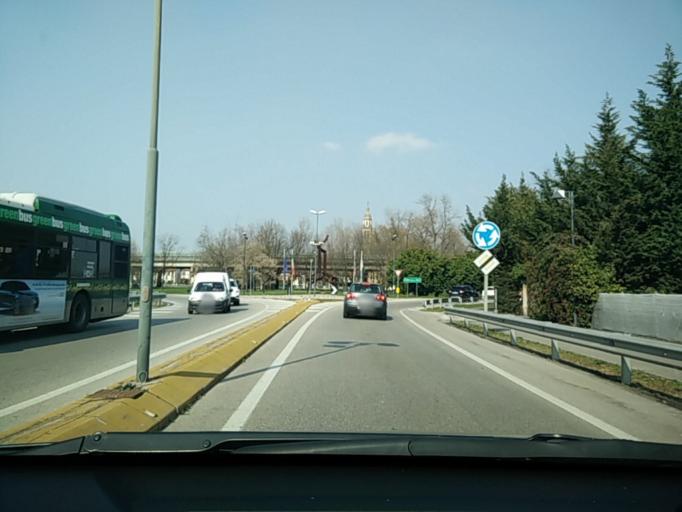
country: IT
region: Veneto
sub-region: Provincia di Treviso
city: Dosson
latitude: 45.6486
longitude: 12.2419
